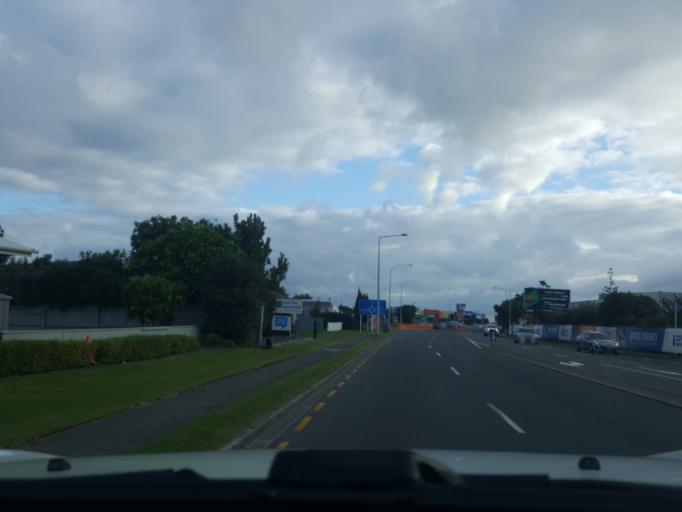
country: NZ
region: Bay of Plenty
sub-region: Tauranga City
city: Tauranga
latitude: -37.6756
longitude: 176.2251
